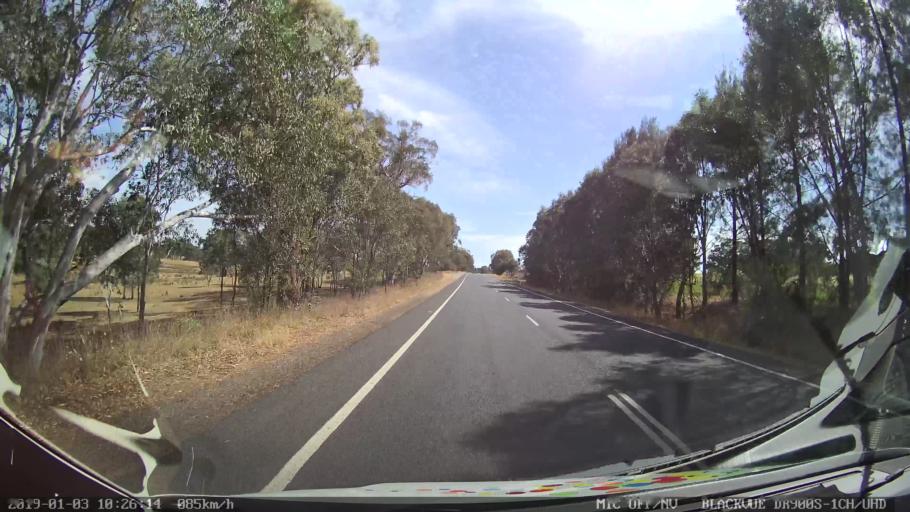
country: AU
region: New South Wales
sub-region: Young
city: Young
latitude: -34.4151
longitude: 148.2481
